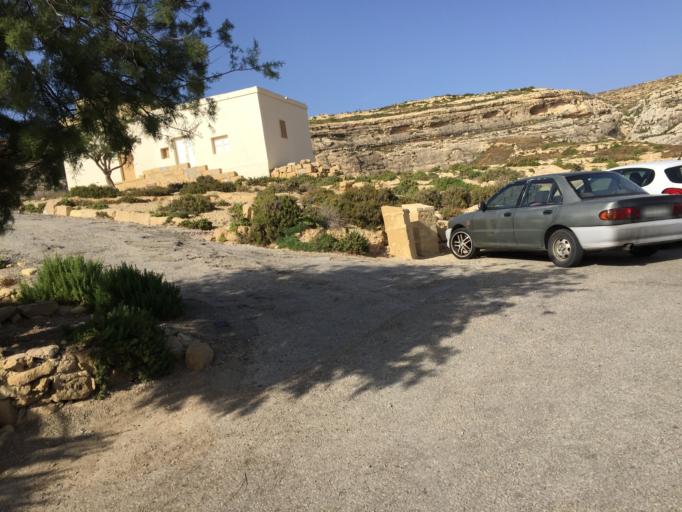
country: MT
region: Saint Lawrence
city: San Lawrenz
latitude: 36.0525
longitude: 14.1900
